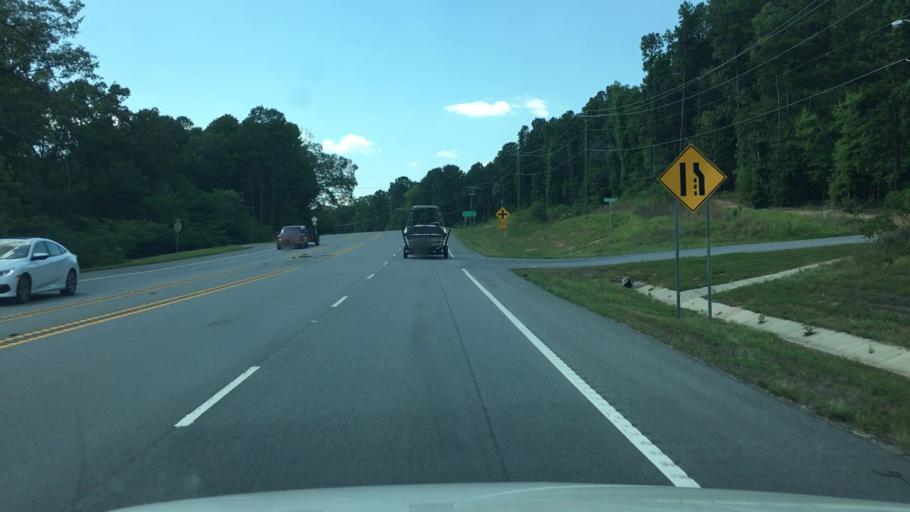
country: US
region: Arkansas
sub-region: Garland County
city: Piney
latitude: 34.5086
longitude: -93.1911
